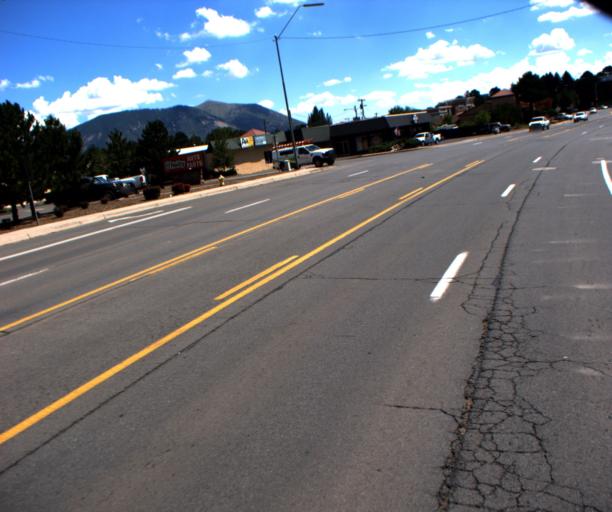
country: US
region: Arizona
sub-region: Coconino County
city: Flagstaff
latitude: 35.1927
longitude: -111.6611
